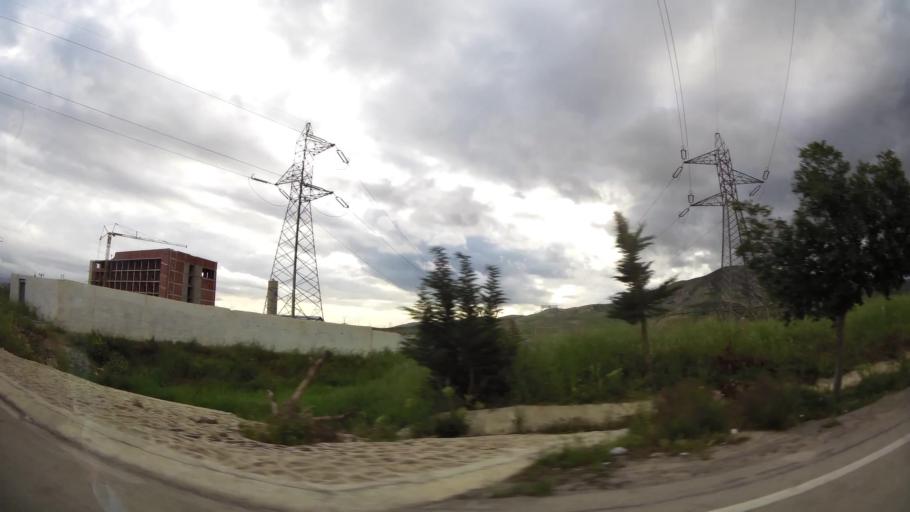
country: MA
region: Taza-Al Hoceima-Taounate
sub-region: Taza
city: Taza
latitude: 34.2684
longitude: -3.9549
